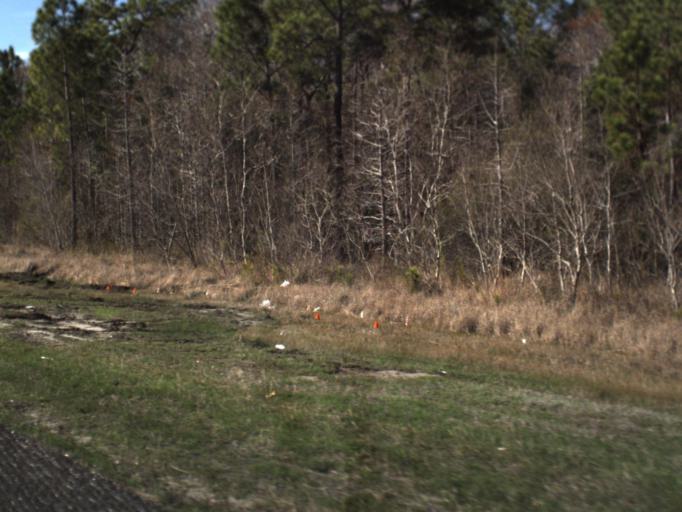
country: US
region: Florida
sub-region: Bay County
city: Panama City Beach
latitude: 30.1897
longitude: -85.7882
